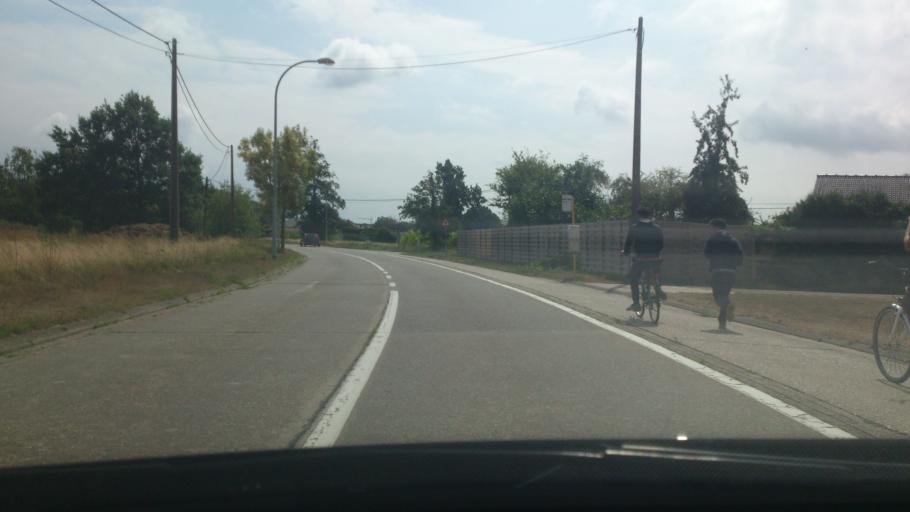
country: BE
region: Flanders
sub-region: Provincie Antwerpen
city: Mol
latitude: 51.2078
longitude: 5.1001
